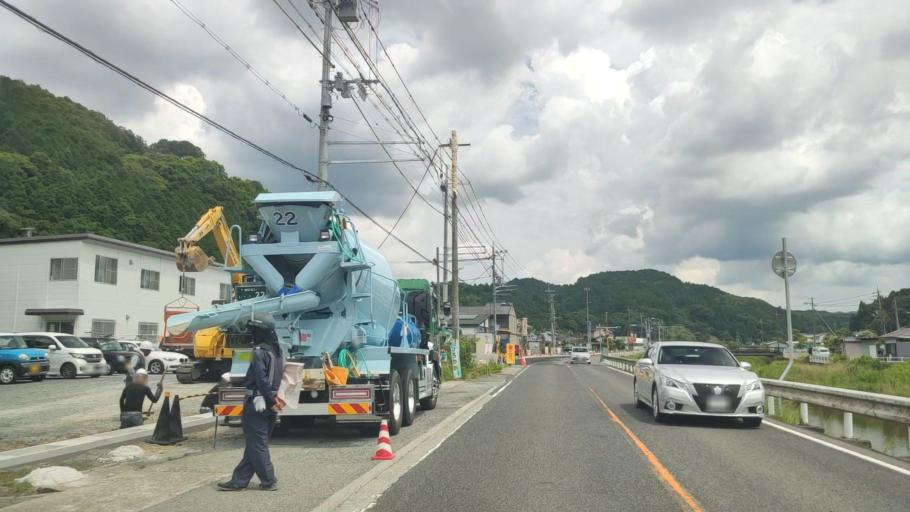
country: JP
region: Hyogo
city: Yamazakicho-nakabirose
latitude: 34.9800
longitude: 134.4416
